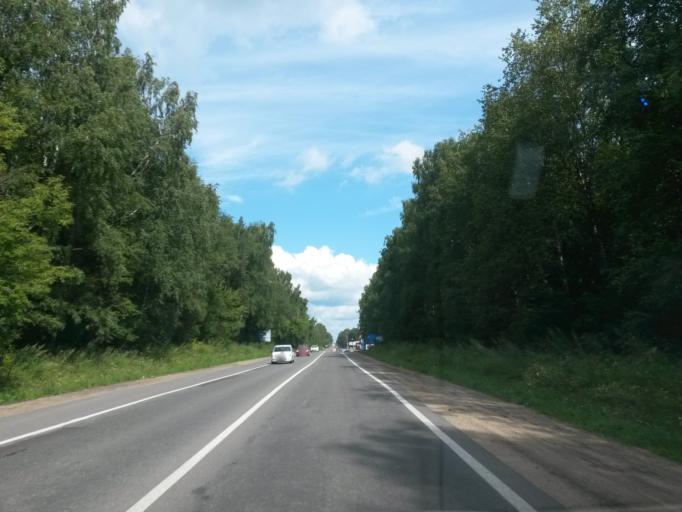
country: RU
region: Jaroslavl
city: Pereslavl'-Zalesskiy
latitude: 56.7781
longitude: 38.8799
